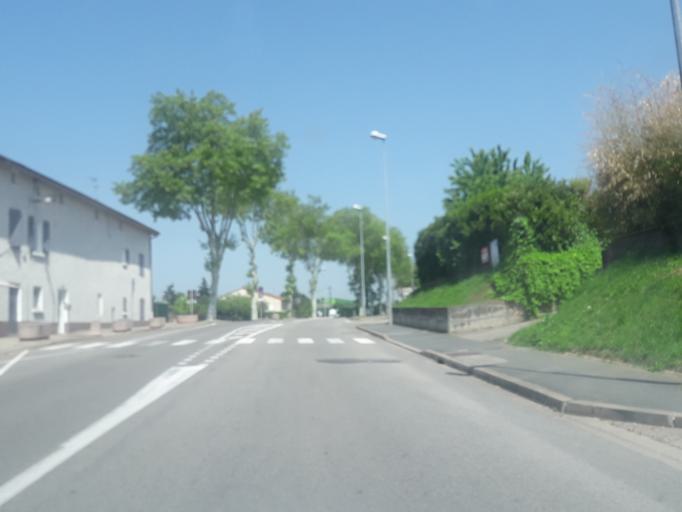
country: FR
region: Rhone-Alpes
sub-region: Departement de l'Ain
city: Mionnay
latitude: 45.8963
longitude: 4.9310
